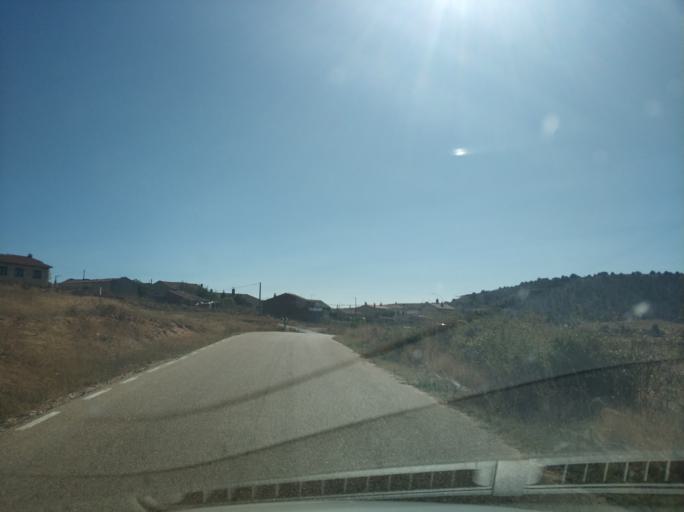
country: ES
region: Castille and Leon
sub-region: Provincia de Soria
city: Santa Maria de las Hoyas
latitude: 41.7722
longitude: -3.1721
